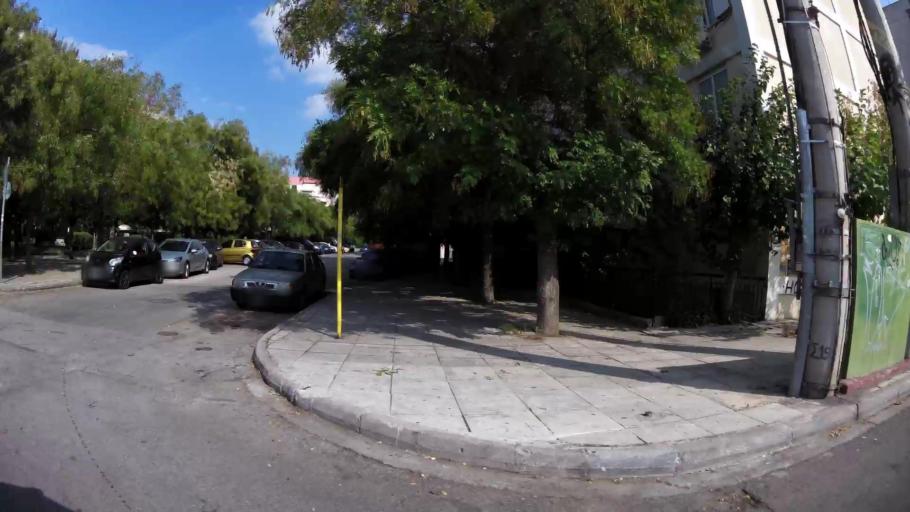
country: GR
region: Attica
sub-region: Nomarchia Athinas
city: Dhafni
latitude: 37.9577
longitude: 23.7228
